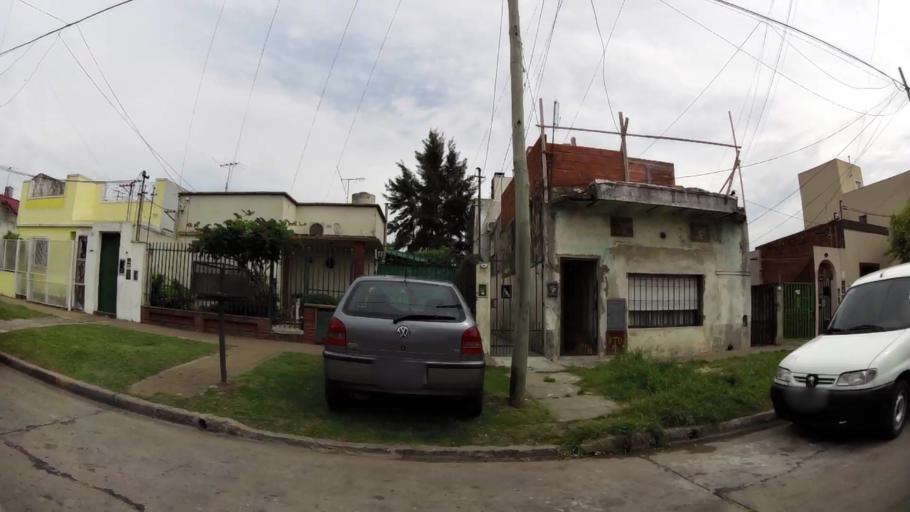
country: AR
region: Buenos Aires F.D.
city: Villa Lugano
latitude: -34.6960
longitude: -58.5136
